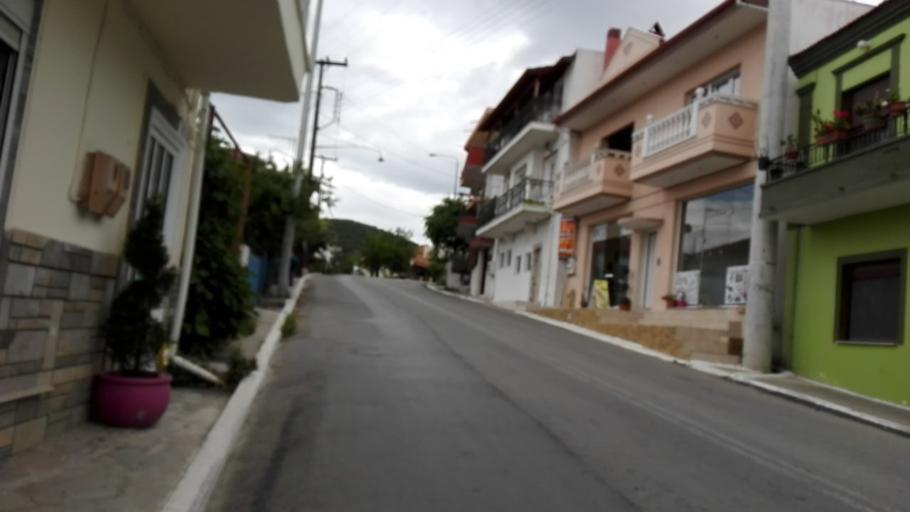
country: GR
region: East Macedonia and Thrace
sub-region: Nomos Kavalas
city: Limenaria
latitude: 40.6274
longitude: 24.5781
